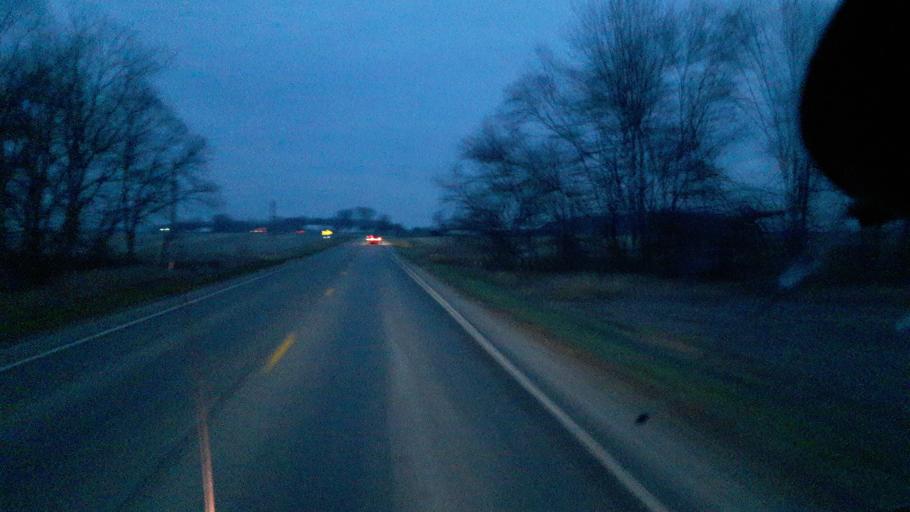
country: US
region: Indiana
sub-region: LaGrange County
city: Lagrange
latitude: 41.6043
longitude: -85.3998
